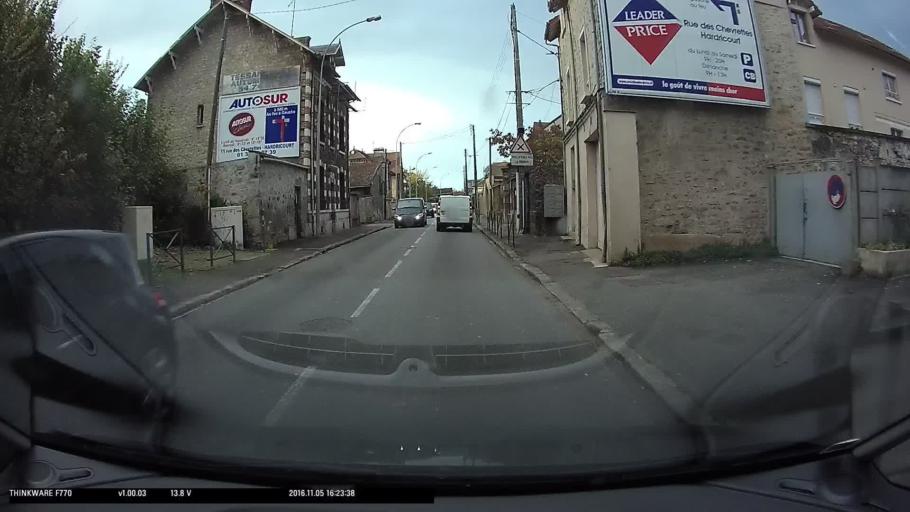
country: FR
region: Ile-de-France
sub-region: Departement des Yvelines
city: Meulan-en-Yvelines
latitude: 49.0064
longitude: 1.9060
